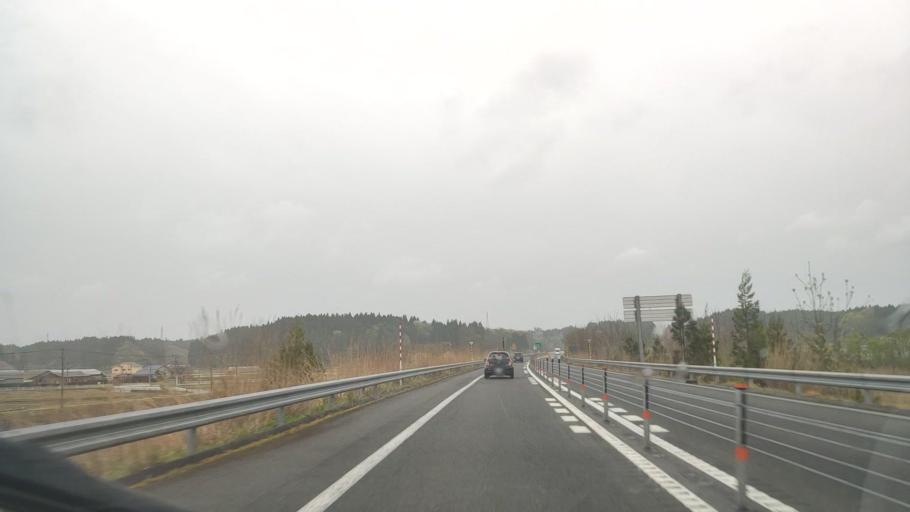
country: JP
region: Akita
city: Noshiromachi
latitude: 40.1874
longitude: 140.0996
